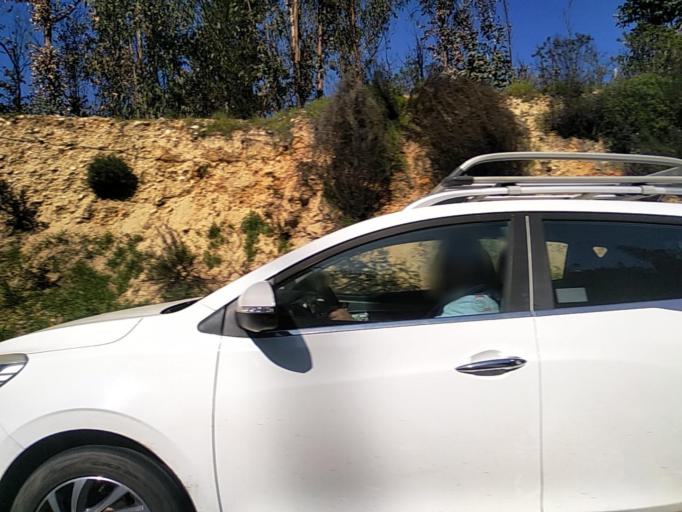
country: CL
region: Valparaiso
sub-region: Provincia de Valparaiso
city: Vina del Mar
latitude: -33.0392
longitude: -71.5043
